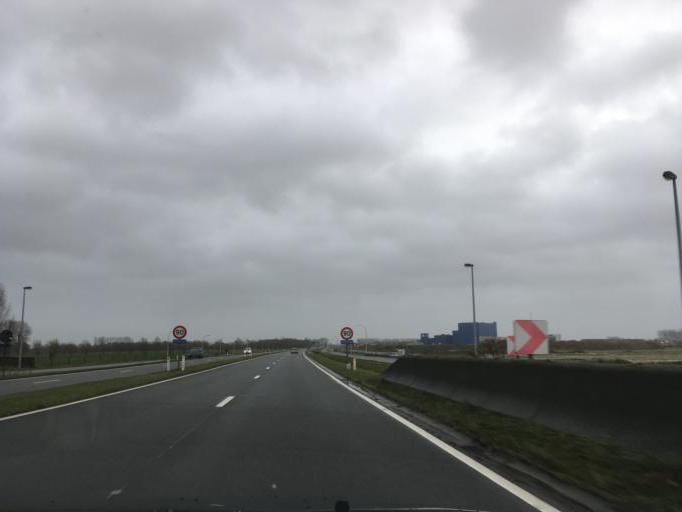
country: BE
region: Flanders
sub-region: Provincie West-Vlaanderen
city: Roeselare
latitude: 50.9792
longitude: 3.1502
